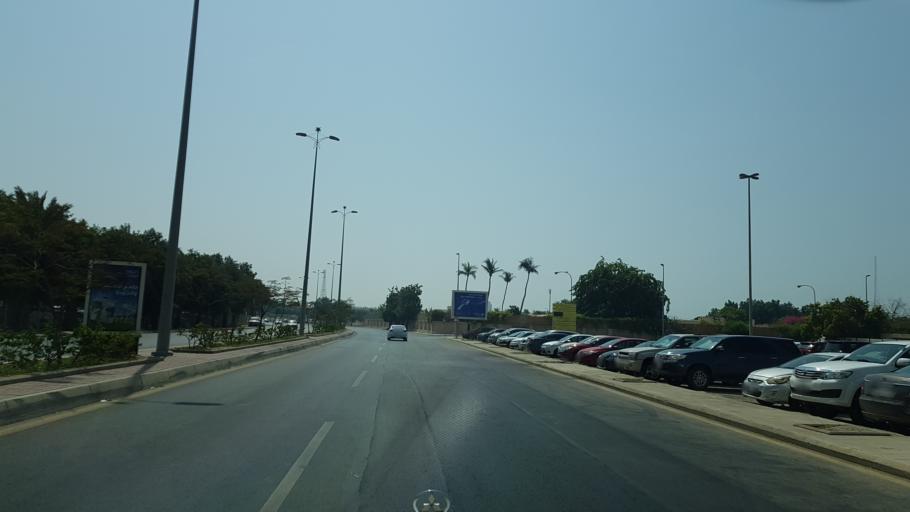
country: SA
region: Makkah
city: Jeddah
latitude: 21.5486
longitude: 39.1528
